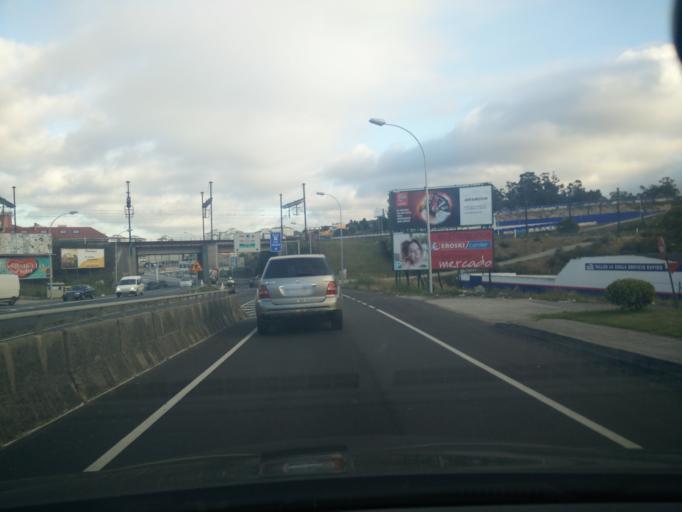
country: ES
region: Galicia
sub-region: Provincia da Coruna
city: A Coruna
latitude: 43.3471
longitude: -8.4194
